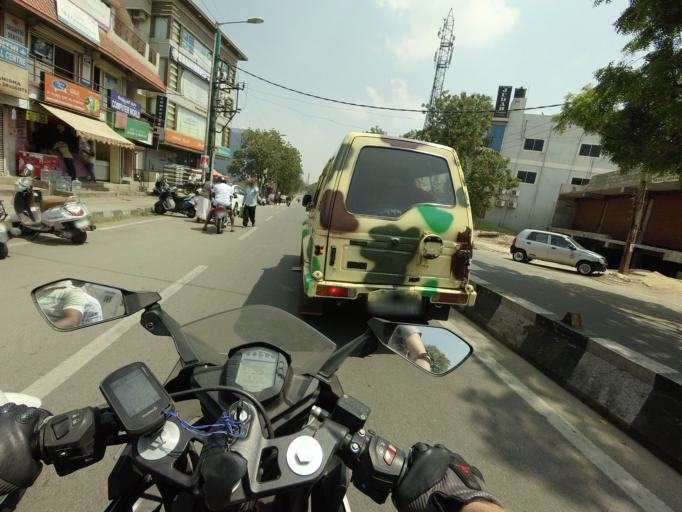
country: IN
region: Karnataka
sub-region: Bangalore Urban
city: Bangalore
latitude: 13.0099
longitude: 77.6431
